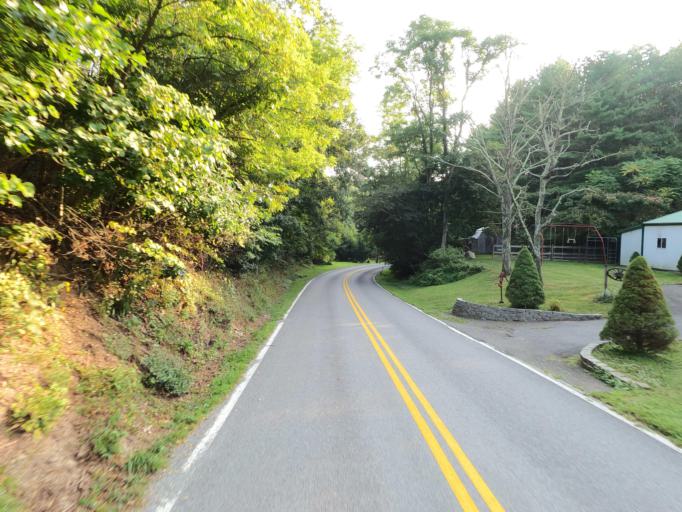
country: US
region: West Virginia
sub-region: Morgan County
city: Berkeley Springs
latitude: 39.6761
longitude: -78.2747
